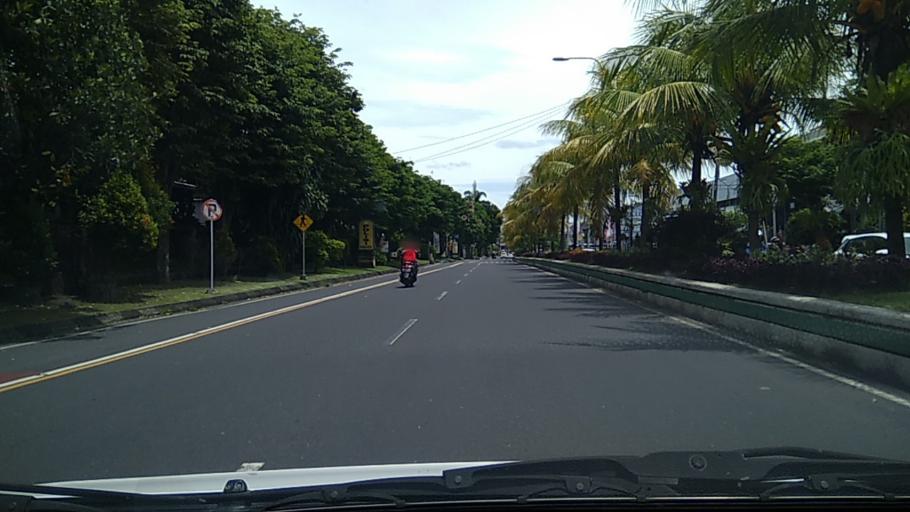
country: ID
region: Bali
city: Tabanan
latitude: -8.5395
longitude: 115.1323
